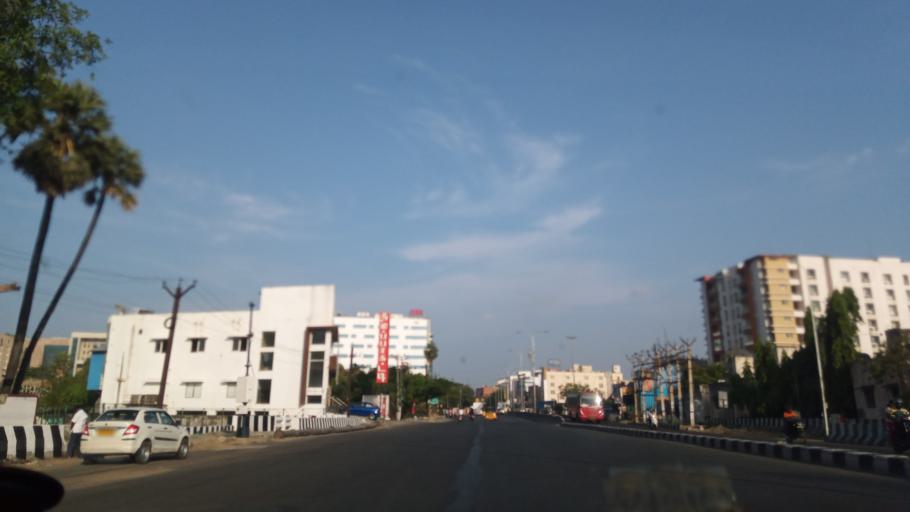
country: IN
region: Tamil Nadu
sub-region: Kancheepuram
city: Manappakkam
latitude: 13.0222
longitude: 80.1817
